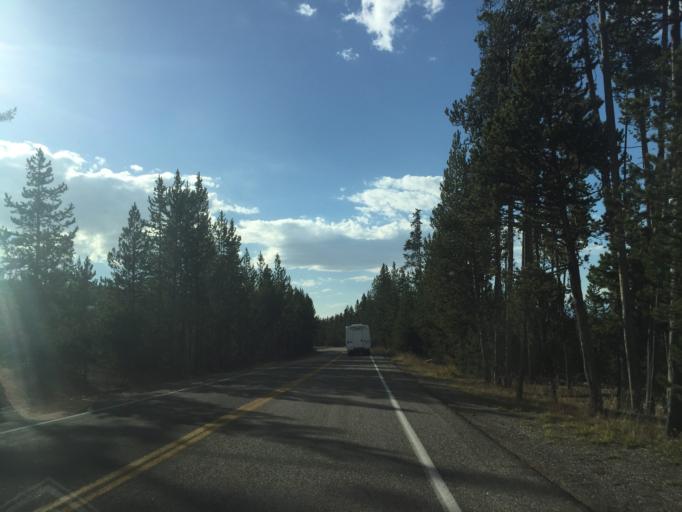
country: US
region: Montana
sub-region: Gallatin County
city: West Yellowstone
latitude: 44.6499
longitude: -111.0068
